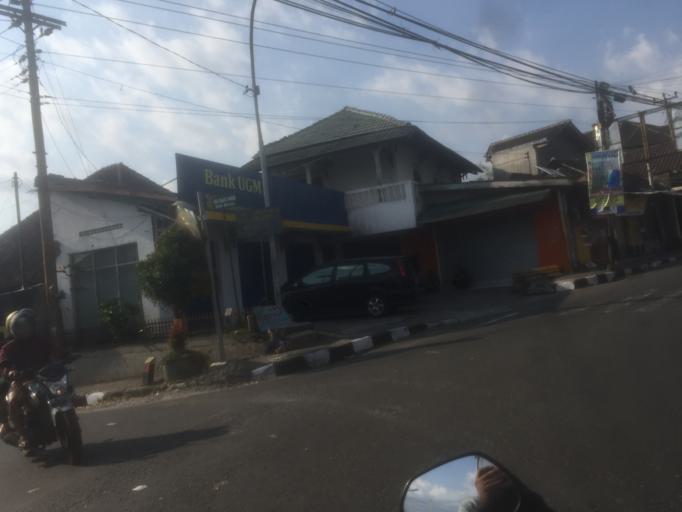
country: ID
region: Daerah Istimewa Yogyakarta
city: Sleman
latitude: -7.6656
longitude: 110.4192
